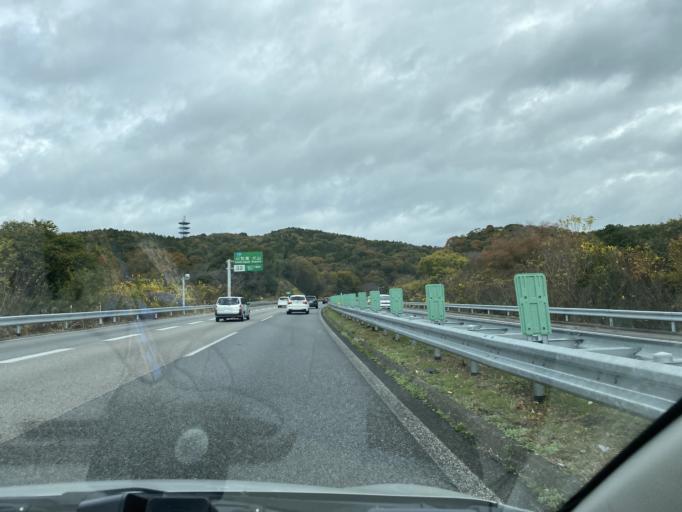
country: JP
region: Aichi
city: Kasugai
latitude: 35.3183
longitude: 137.0199
